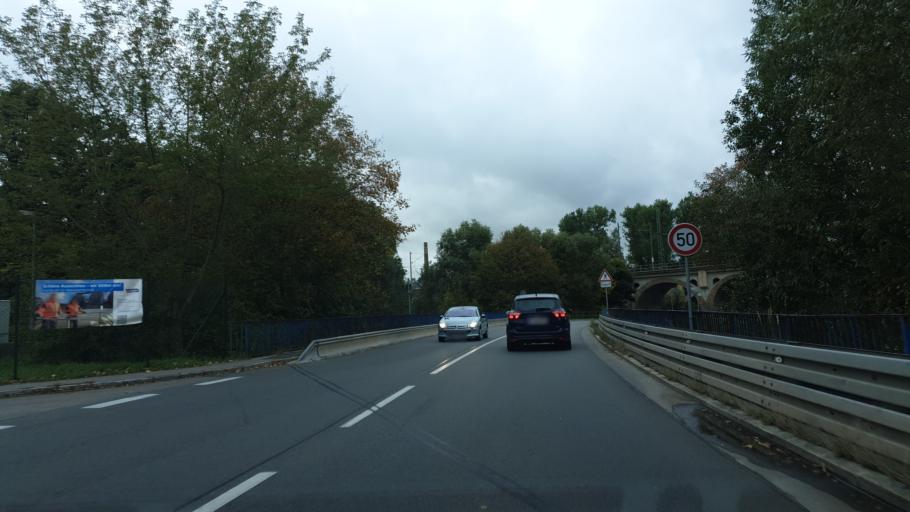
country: DE
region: Saxony
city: Glauchau
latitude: 50.8285
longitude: 12.5563
